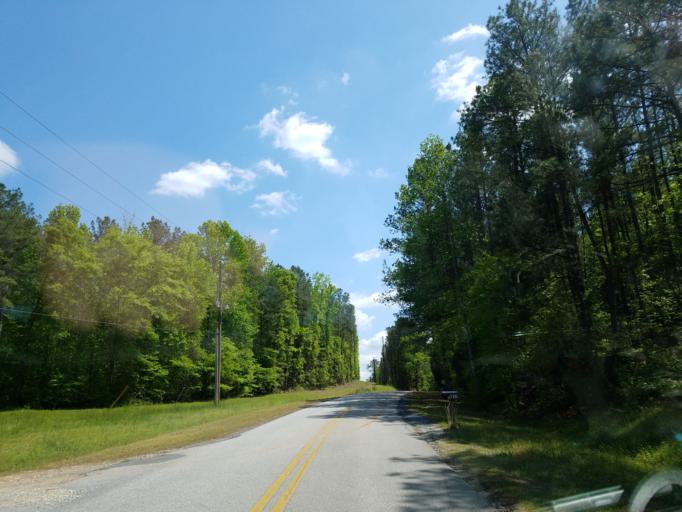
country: US
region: Georgia
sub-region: Monroe County
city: Forsyth
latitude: 33.1267
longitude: -83.9694
